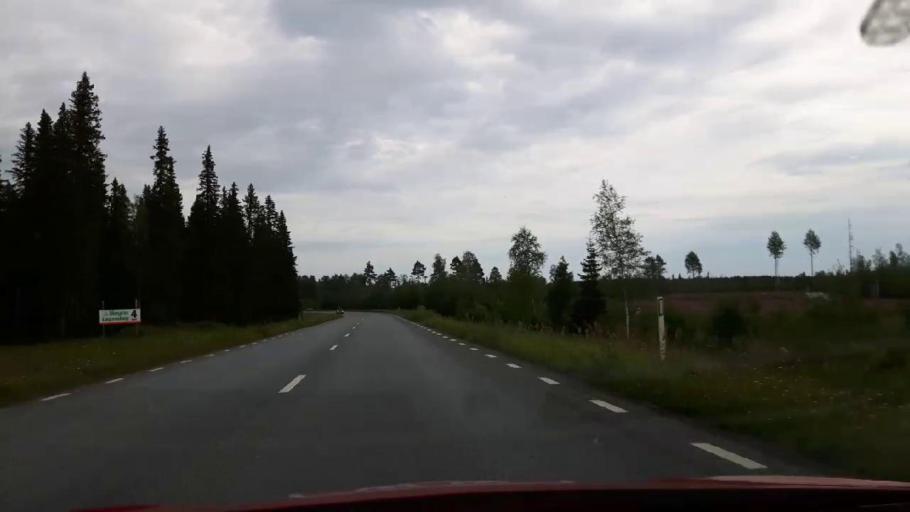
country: SE
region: Jaemtland
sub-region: Stroemsunds Kommun
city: Stroemsund
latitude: 63.5405
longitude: 15.3637
